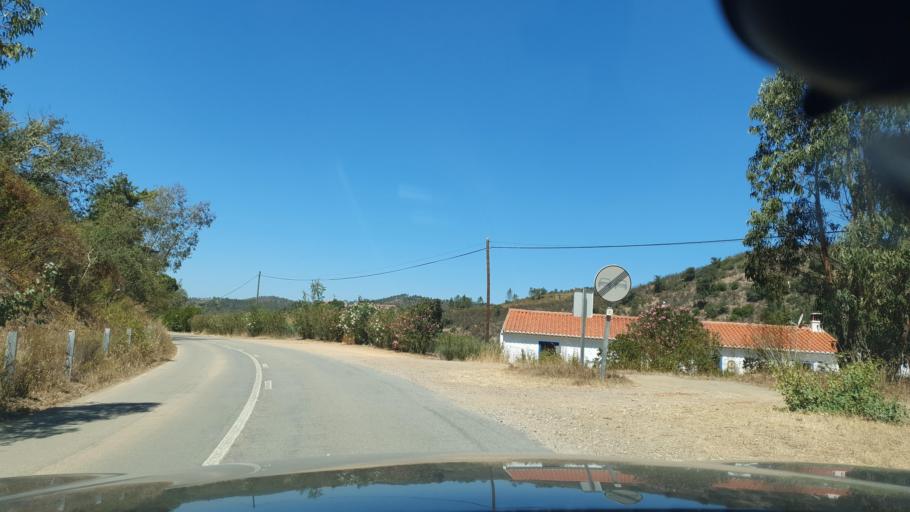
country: PT
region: Beja
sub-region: Odemira
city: Odemira
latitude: 37.5104
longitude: -8.4625
